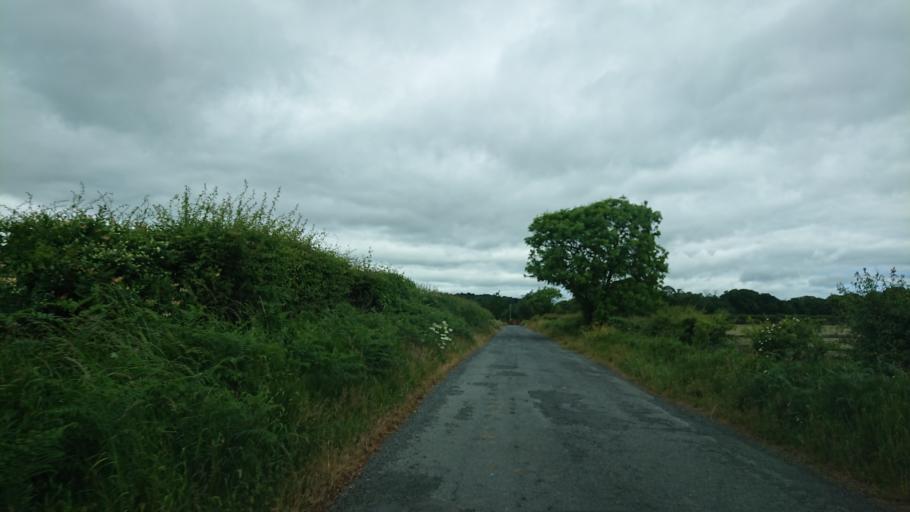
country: IE
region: Munster
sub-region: Waterford
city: Waterford
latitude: 52.2238
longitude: -7.1454
